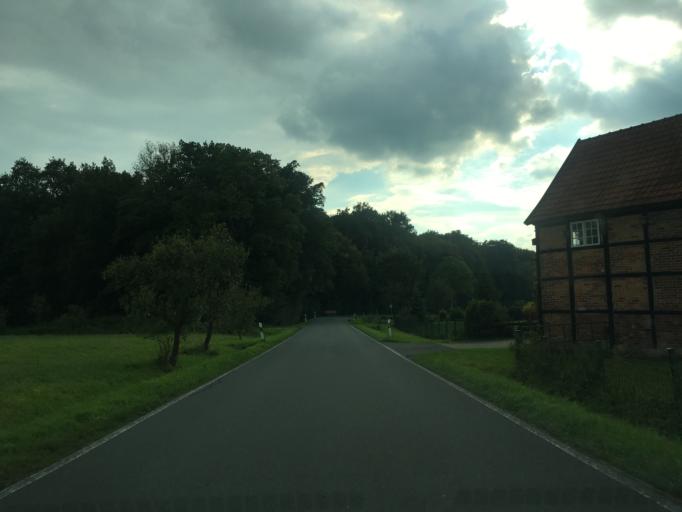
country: DE
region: North Rhine-Westphalia
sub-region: Regierungsbezirk Munster
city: Nordkirchen
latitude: 51.7440
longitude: 7.5527
